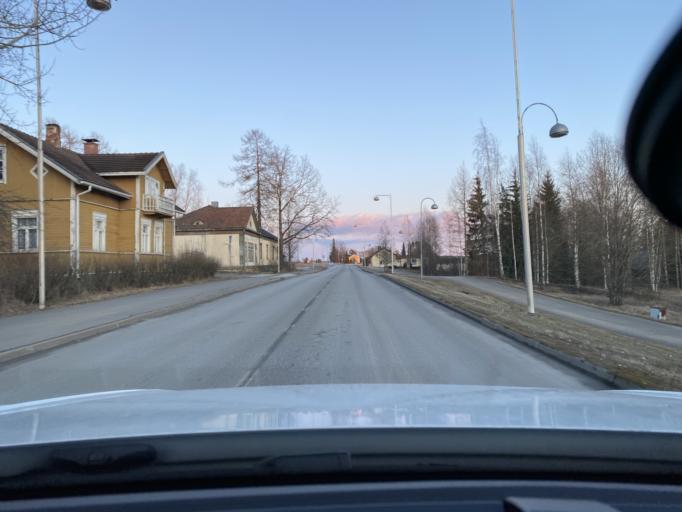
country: FI
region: Pirkanmaa
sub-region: Lounais-Pirkanmaa
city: Punkalaidun
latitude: 61.1087
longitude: 23.1269
